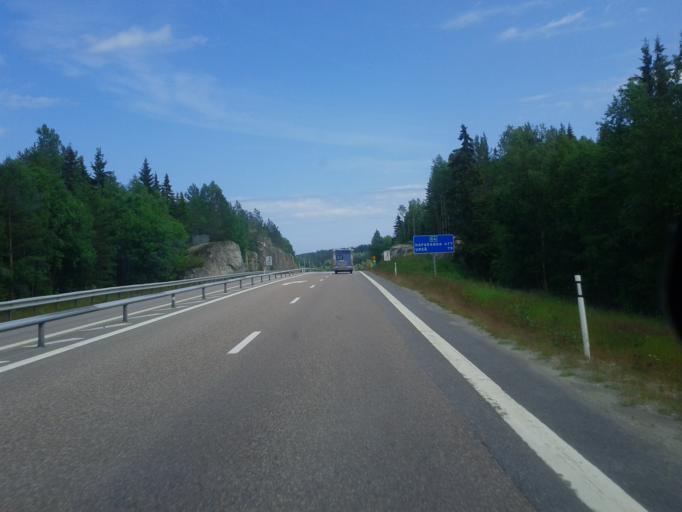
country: SE
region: Vaesternorrland
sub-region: OErnskoeldsviks Kommun
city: Husum
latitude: 63.3508
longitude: 19.1518
